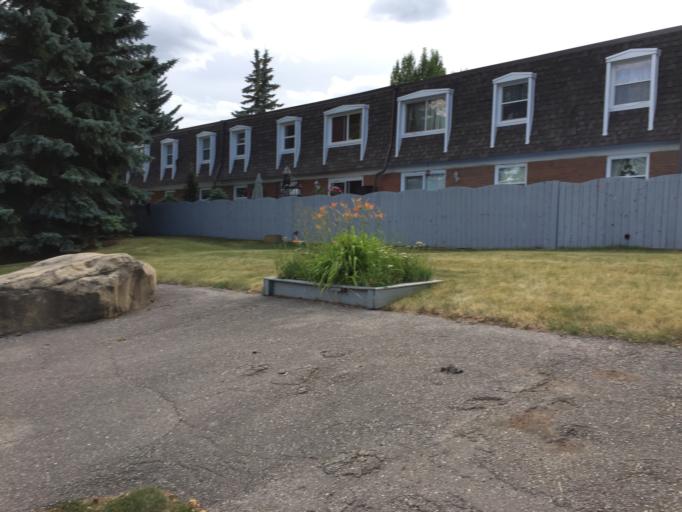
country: CA
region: Alberta
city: Calgary
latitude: 50.9487
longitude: -114.0832
